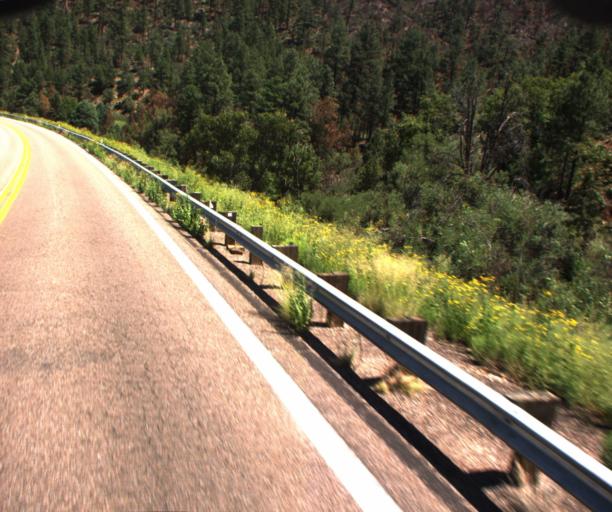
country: US
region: Arizona
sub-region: Navajo County
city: Linden
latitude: 34.0685
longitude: -110.1962
